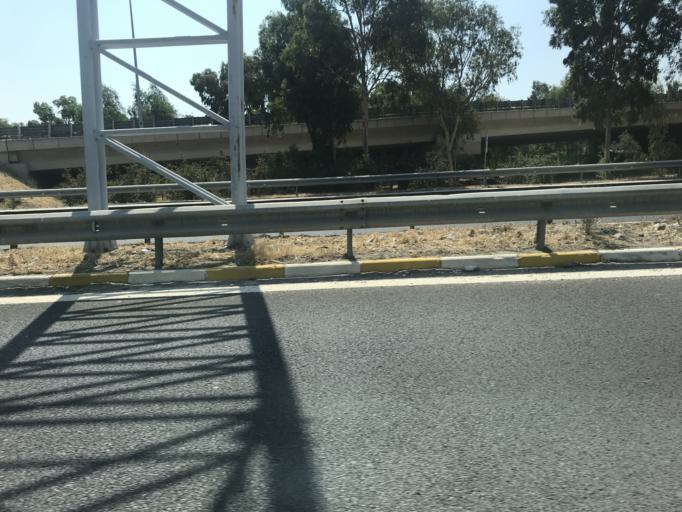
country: TR
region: Izmir
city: Karsiyaka
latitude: 38.3986
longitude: 27.0636
